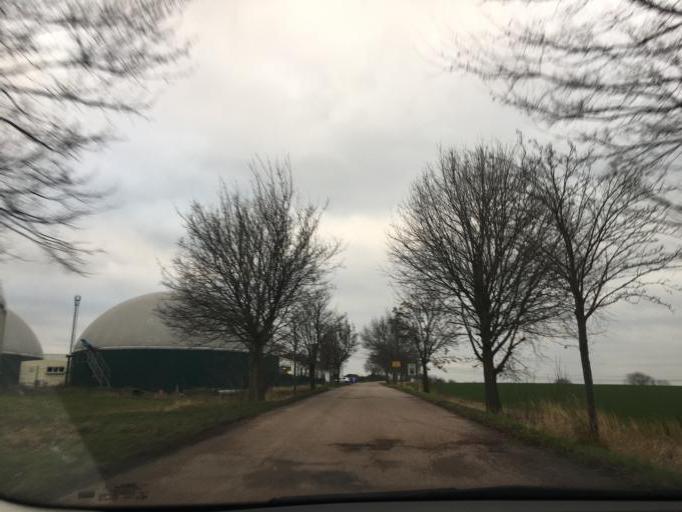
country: DE
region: Saxony
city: Niederfrohna
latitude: 50.8813
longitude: 12.7101
